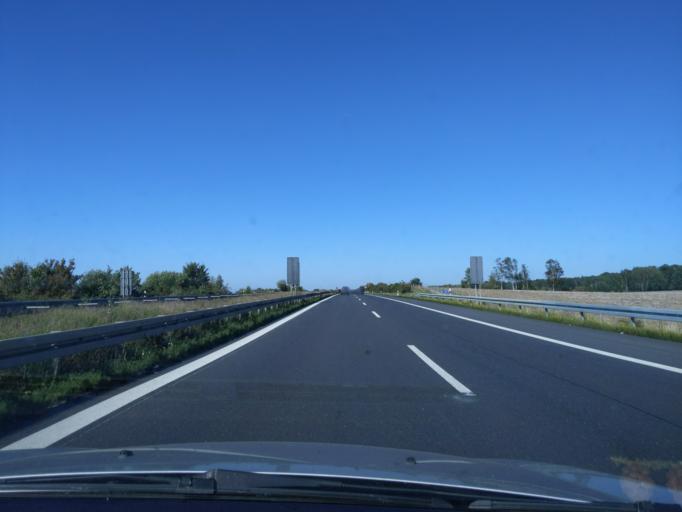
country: DE
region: Saxony
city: Wachau
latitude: 51.1650
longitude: 13.9224
